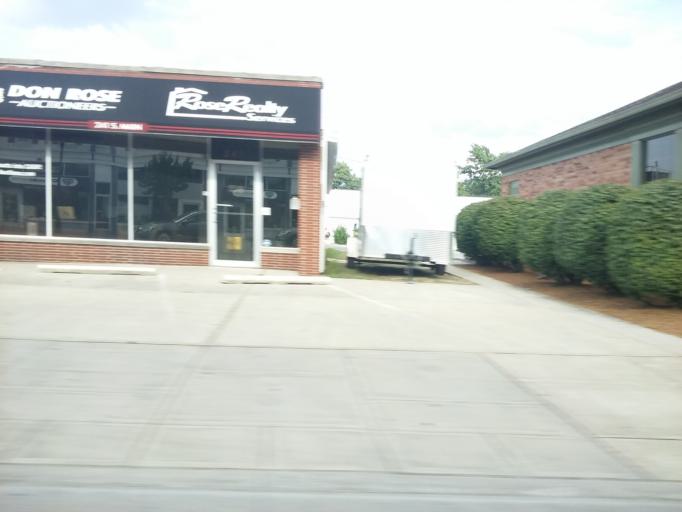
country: US
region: Ohio
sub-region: Wood County
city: Bowling Green
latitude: 41.3725
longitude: -83.6502
